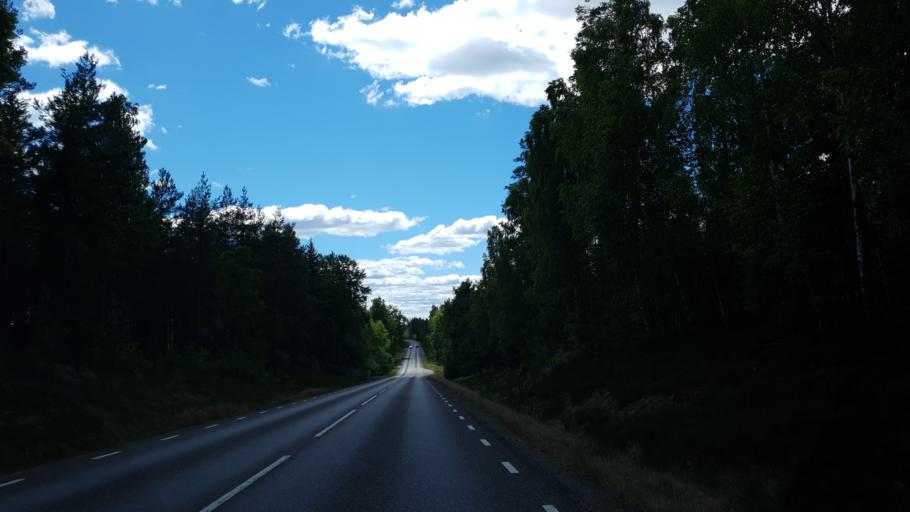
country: SE
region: Kronoberg
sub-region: Lessebo Kommun
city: Lessebo
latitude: 56.7862
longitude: 15.3106
